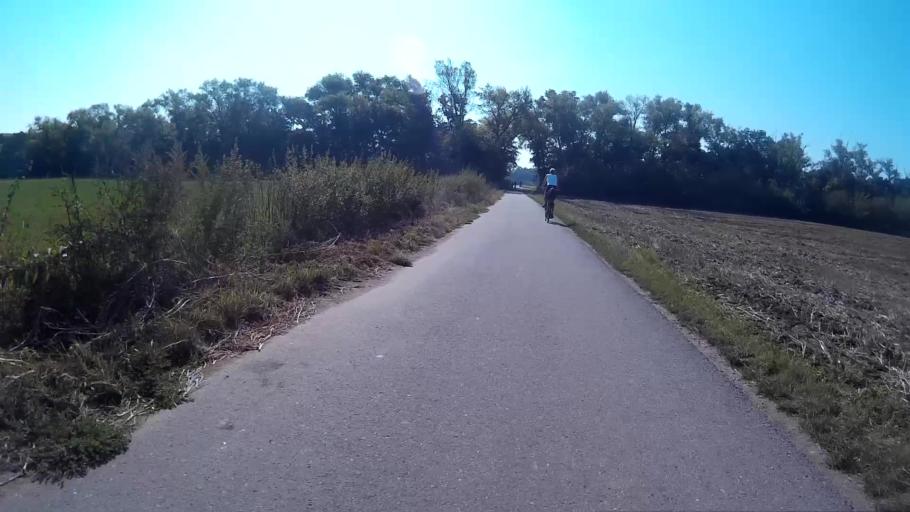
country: CZ
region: South Moravian
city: Drnholec
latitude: 48.8666
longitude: 16.5311
